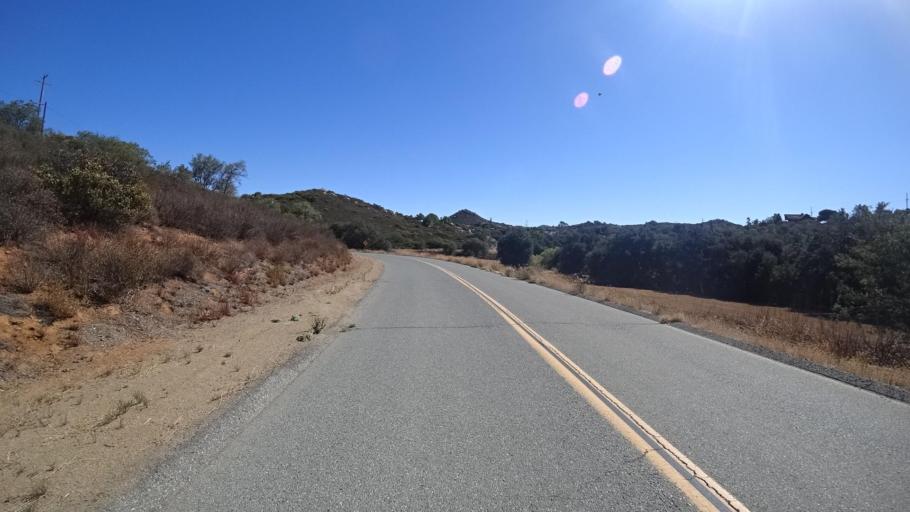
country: US
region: California
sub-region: San Diego County
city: Descanso
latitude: 32.7899
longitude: -116.6656
